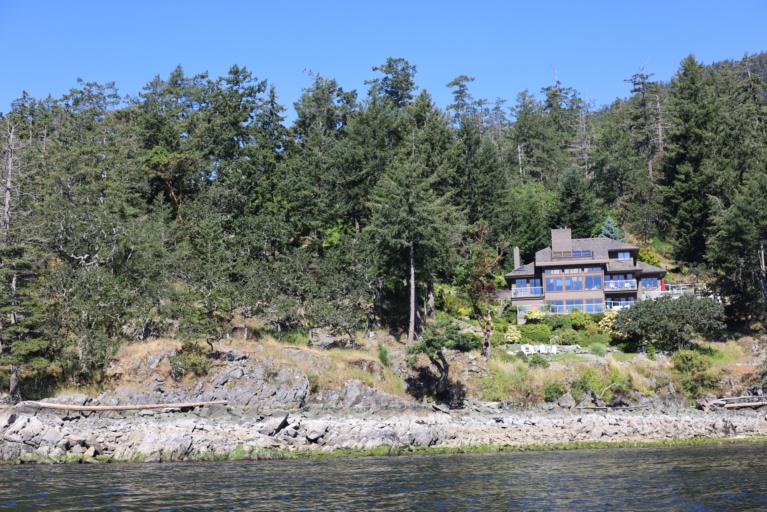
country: CA
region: British Columbia
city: North Cowichan
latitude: 48.8228
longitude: -123.5847
